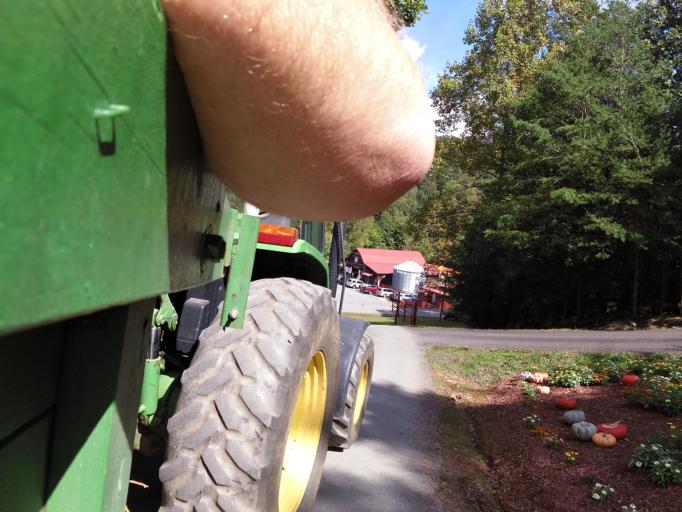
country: US
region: Georgia
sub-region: Dawson County
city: Dawsonville
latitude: 34.5509
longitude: -84.2570
